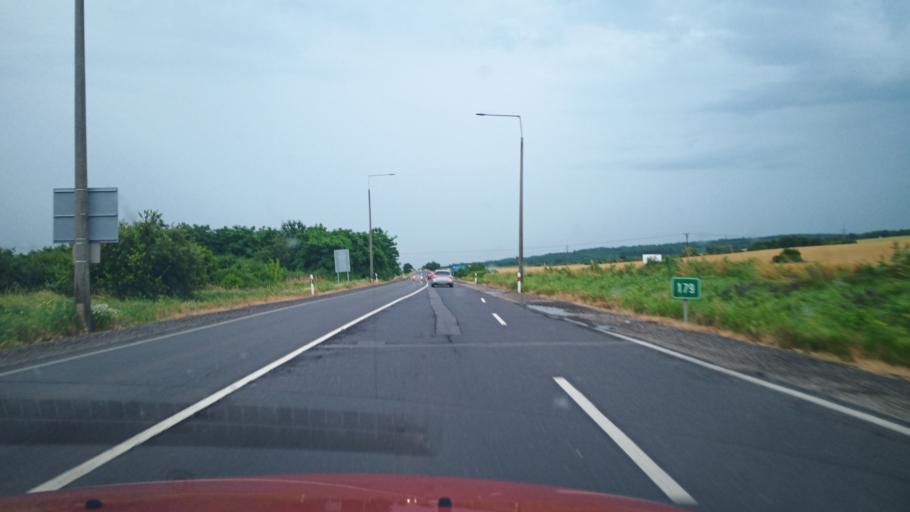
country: HU
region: Borsod-Abauj-Zemplen
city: Malyi
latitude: 48.0490
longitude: 20.8004
